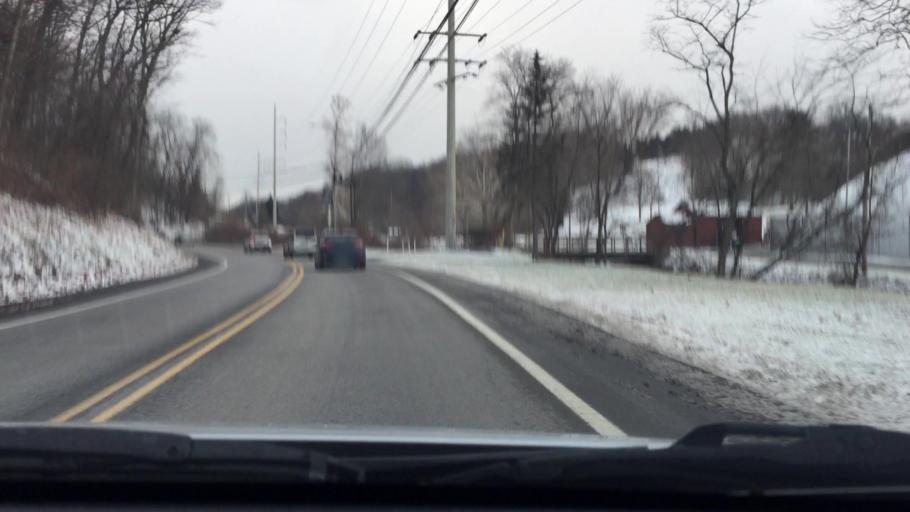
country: US
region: Pennsylvania
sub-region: Allegheny County
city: Upper Saint Clair
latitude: 40.3390
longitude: -80.0778
